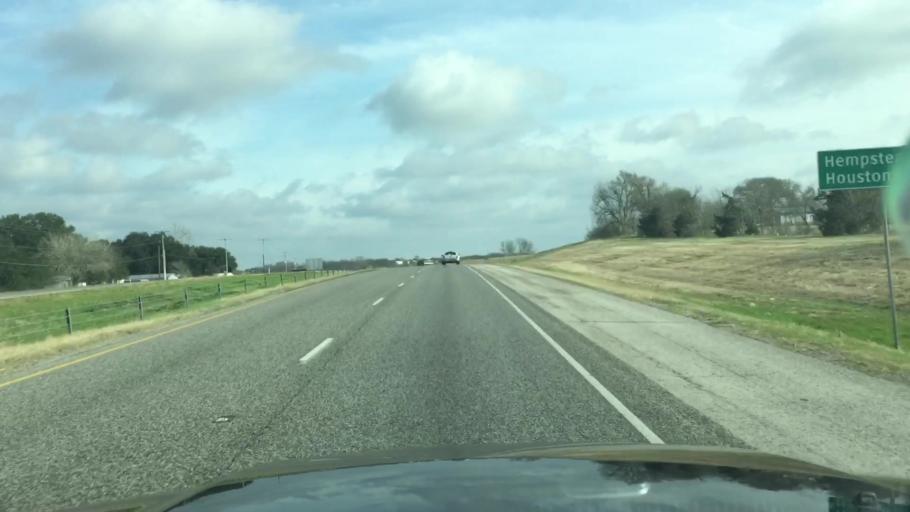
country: US
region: Texas
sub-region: Washington County
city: Brenham
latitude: 30.1395
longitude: -96.3550
